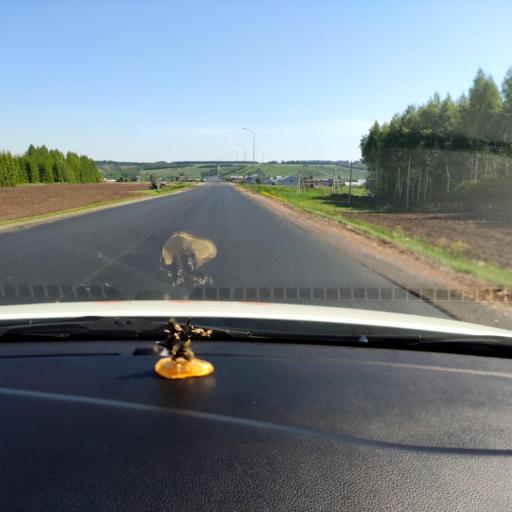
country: RU
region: Tatarstan
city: Vysokaya Gora
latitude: 56.1128
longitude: 49.1864
